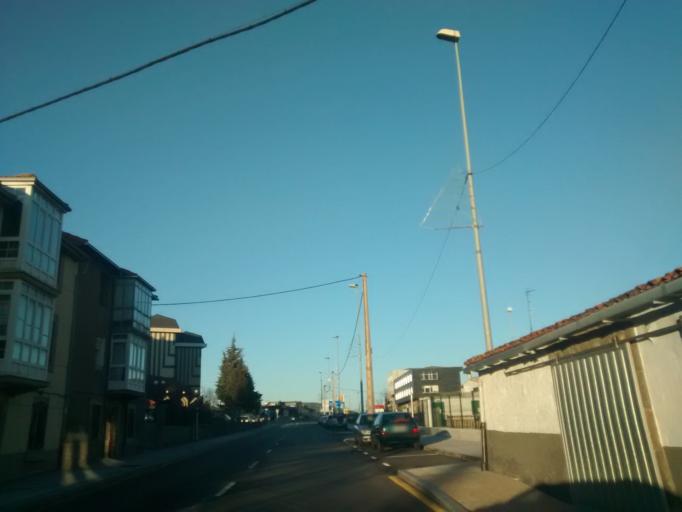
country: ES
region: Cantabria
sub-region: Provincia de Cantabria
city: Reinosa
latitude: 43.0047
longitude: -4.1306
